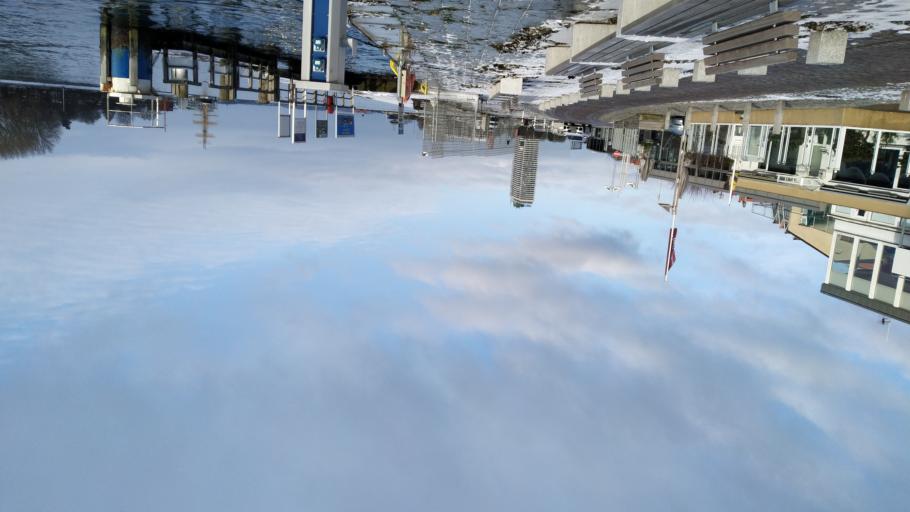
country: DE
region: Schleswig-Holstein
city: Travemuende
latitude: 53.9563
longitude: 10.8691
